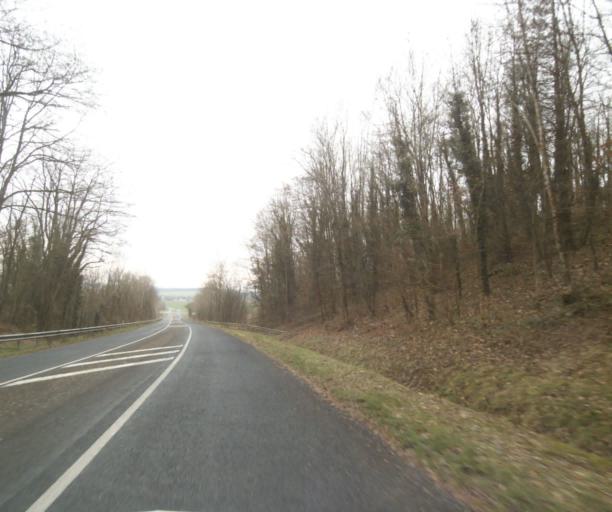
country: FR
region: Champagne-Ardenne
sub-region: Departement de la Haute-Marne
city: Bienville
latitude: 48.5702
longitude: 5.0363
